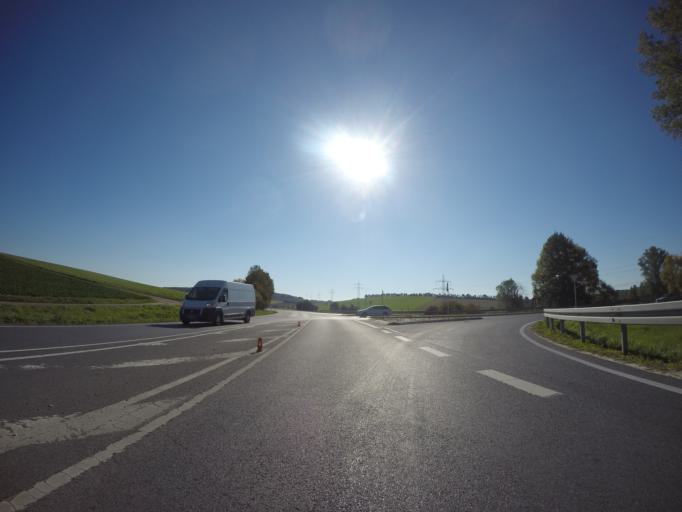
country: DE
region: Bavaria
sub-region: Regierungsbezirk Unterfranken
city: Waldbrunn
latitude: 49.7753
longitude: 9.7770
